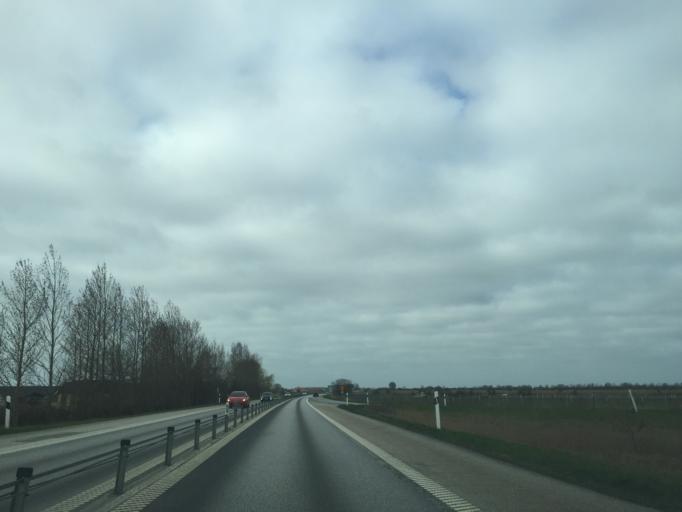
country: SE
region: Skane
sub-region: Vellinge Kommun
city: Hollviken
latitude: 55.4366
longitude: 12.9829
